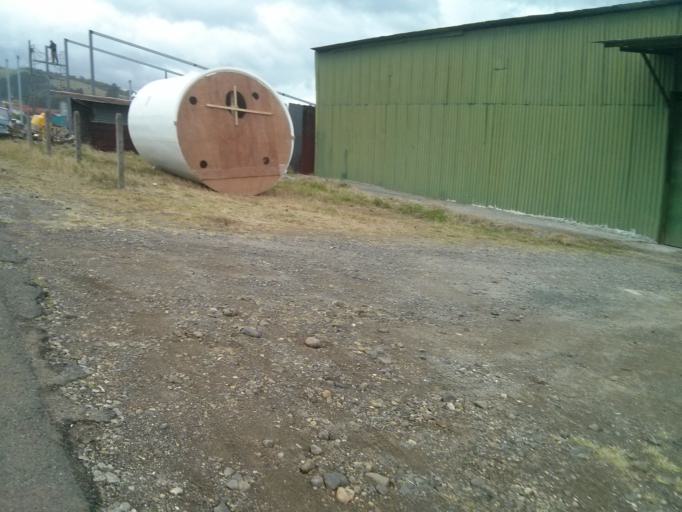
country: CR
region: Cartago
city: Cartago
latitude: 9.8911
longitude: -83.9411
